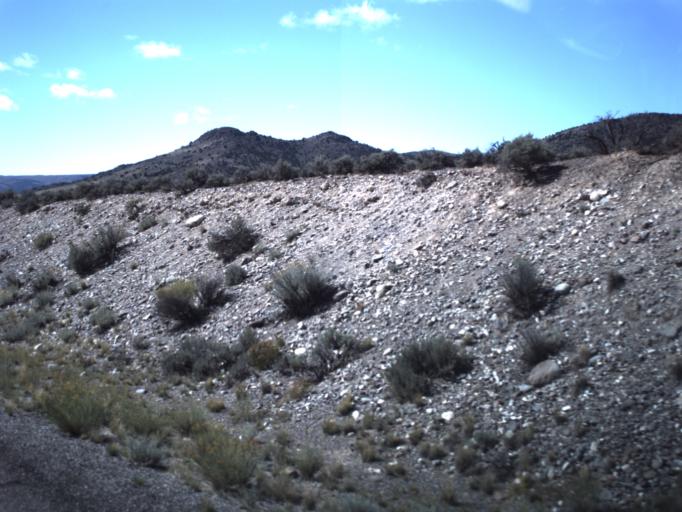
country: US
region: Utah
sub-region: Piute County
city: Junction
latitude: 38.3217
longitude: -111.9632
